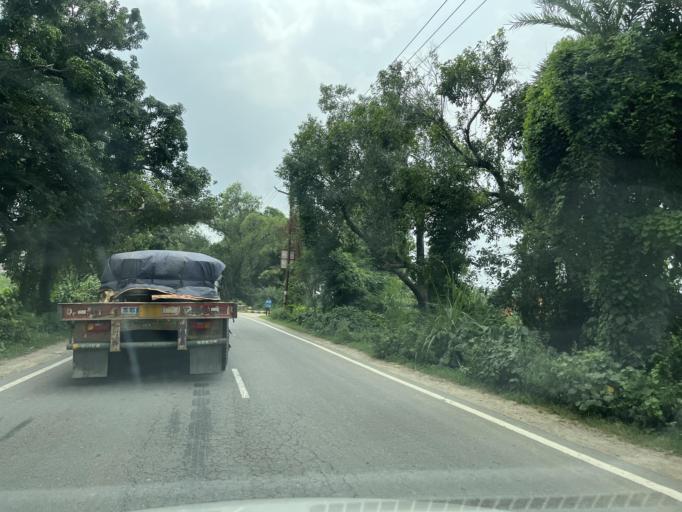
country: IN
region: Uttar Pradesh
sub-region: Bijnor
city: Najibabad
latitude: 29.5884
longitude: 78.3386
